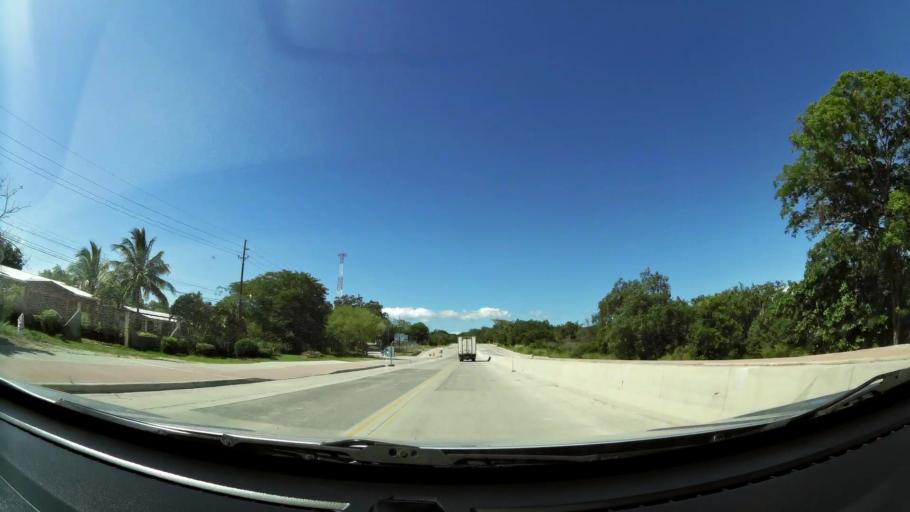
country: CR
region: Guanacaste
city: Liberia
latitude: 10.5678
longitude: -85.3916
